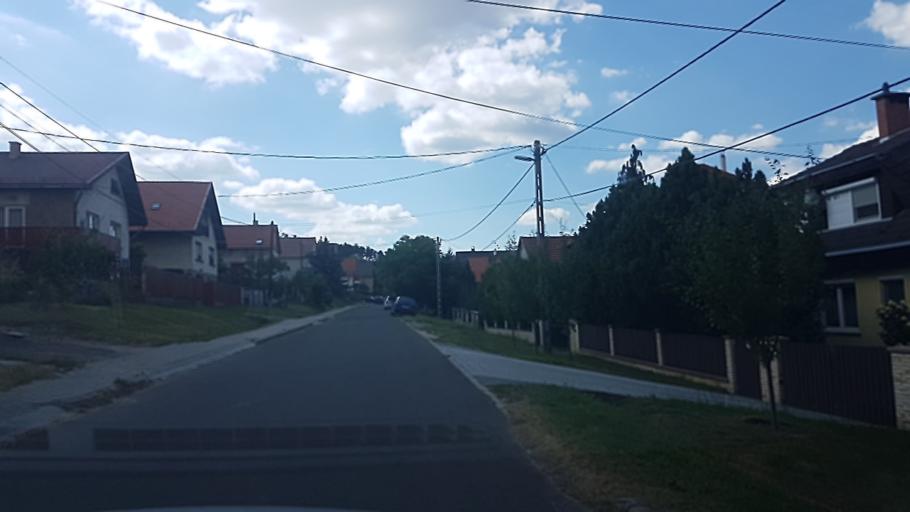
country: HU
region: Pest
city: Pilisszentivan
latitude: 47.6074
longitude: 18.8928
